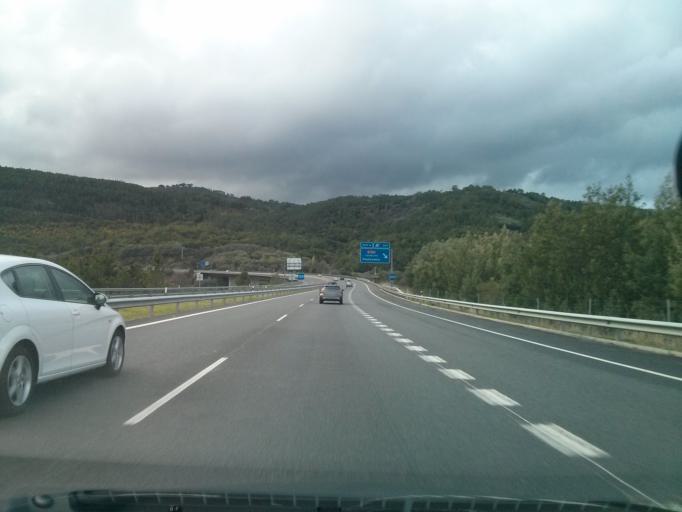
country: ES
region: Galicia
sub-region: Provincia de Ourense
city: Punxin
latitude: 42.3418
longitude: -8.0013
